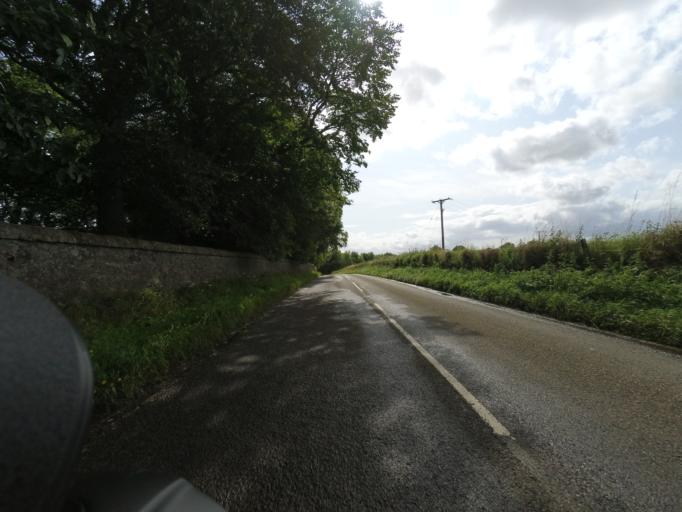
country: GB
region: Scotland
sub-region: Highland
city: Tain
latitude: 57.7364
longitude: -4.0822
